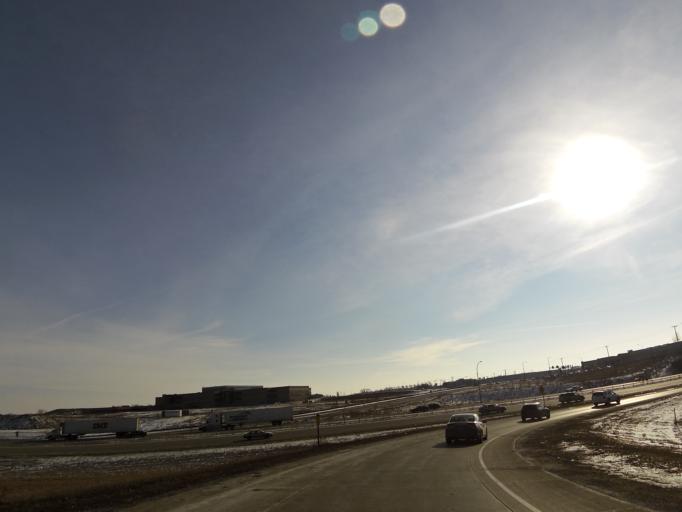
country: US
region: Minnesota
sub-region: Washington County
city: Oakdale
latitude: 44.9497
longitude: -92.9320
